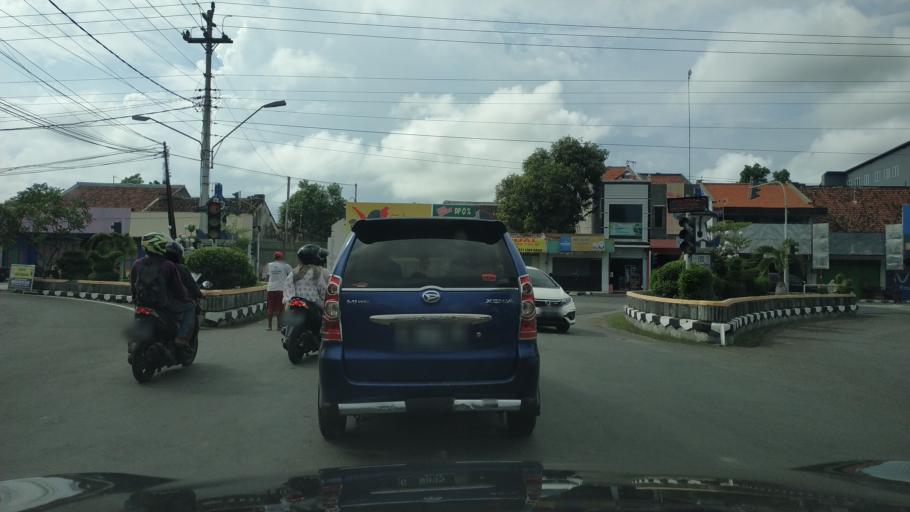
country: ID
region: Central Java
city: Pemalang
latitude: -6.8902
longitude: 109.3824
